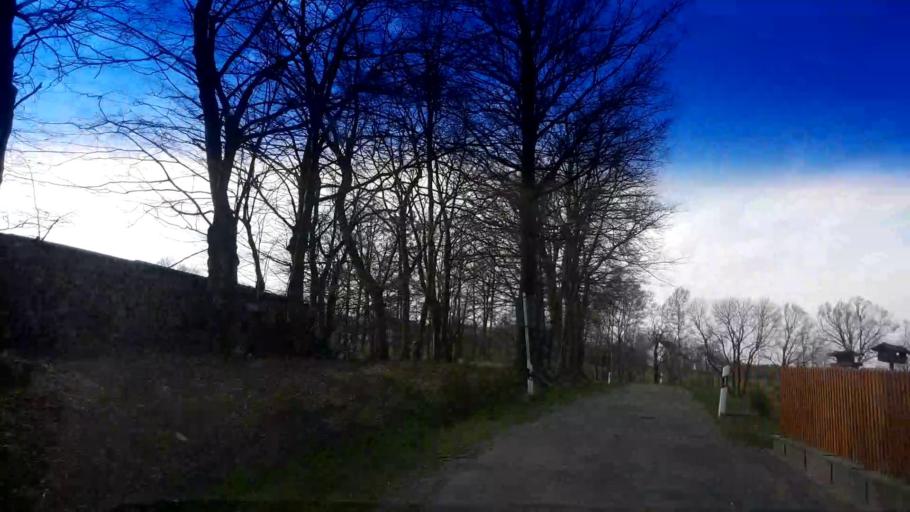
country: DE
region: Bavaria
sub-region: Upper Franconia
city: Himmelkron
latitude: 50.0274
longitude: 11.6189
